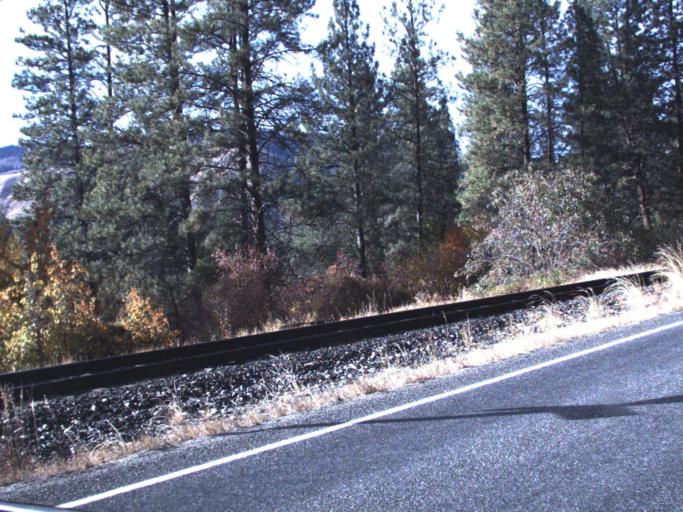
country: US
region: Washington
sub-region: Stevens County
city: Kettle Falls
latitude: 48.6963
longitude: -118.0135
